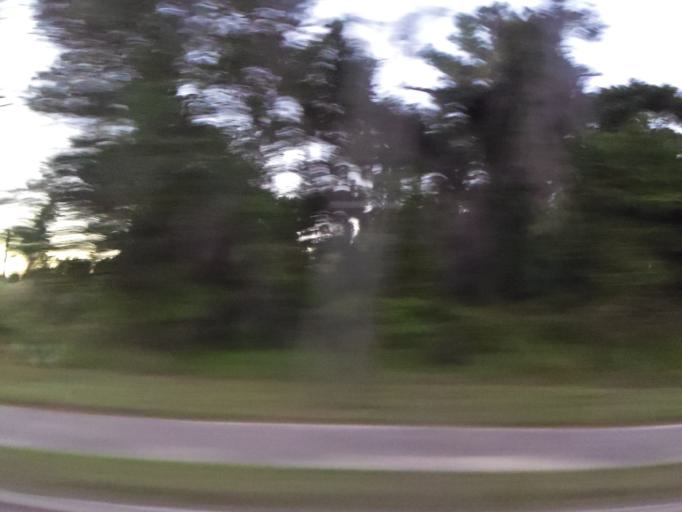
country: US
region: Florida
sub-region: Saint Johns County
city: Palm Valley
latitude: 30.0672
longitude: -81.4943
